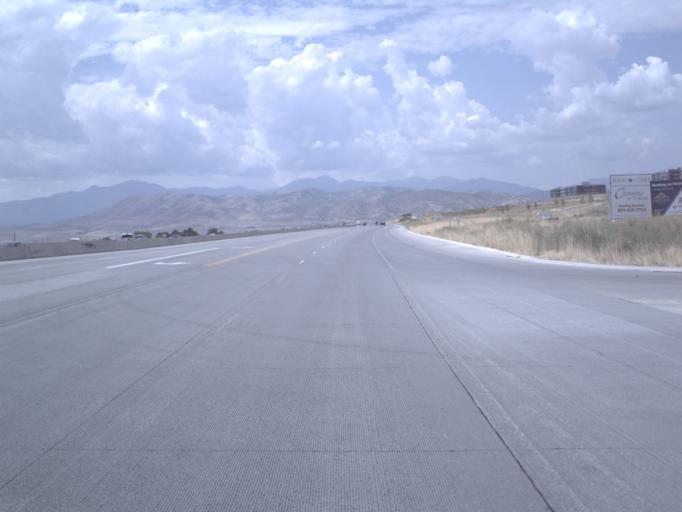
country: US
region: Utah
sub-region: Utah County
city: Lehi
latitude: 40.4326
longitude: -111.8570
